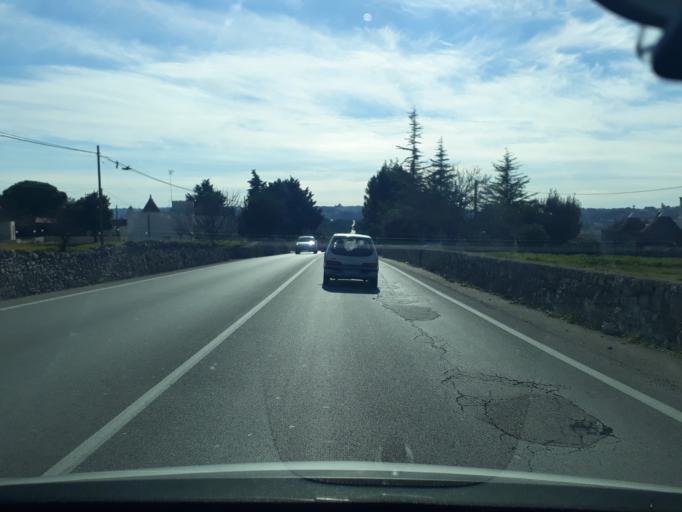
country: IT
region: Apulia
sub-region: Provincia di Bari
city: Locorotondo
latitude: 40.7417
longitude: 17.3323
